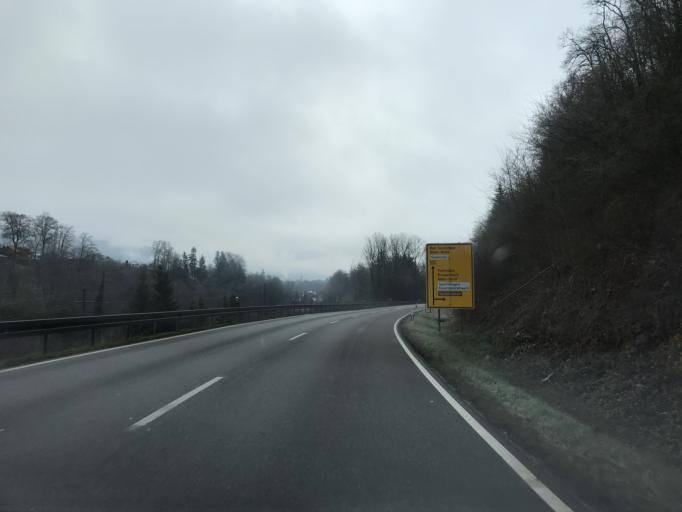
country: DE
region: Baden-Wuerttemberg
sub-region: Freiburg Region
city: Wehr
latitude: 47.6391
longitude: 7.8949
